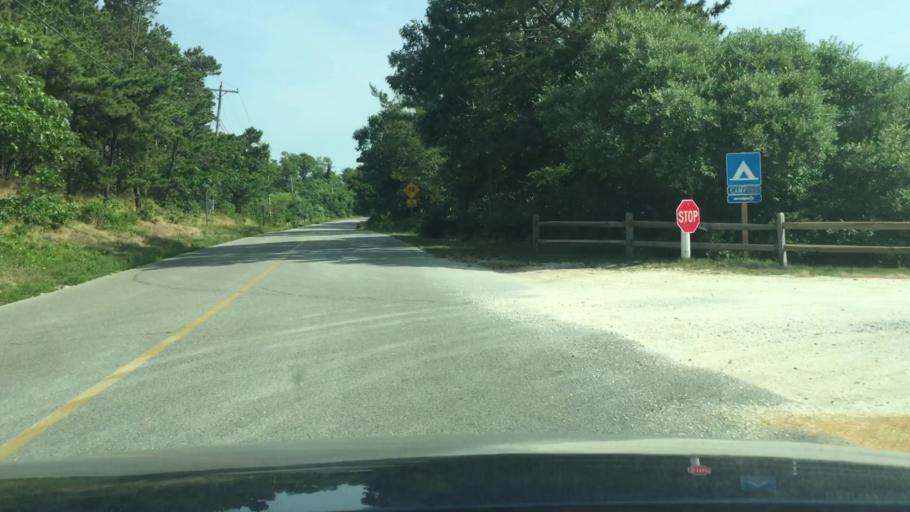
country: US
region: Massachusetts
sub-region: Barnstable County
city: Truro
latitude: 42.0358
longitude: -70.0661
